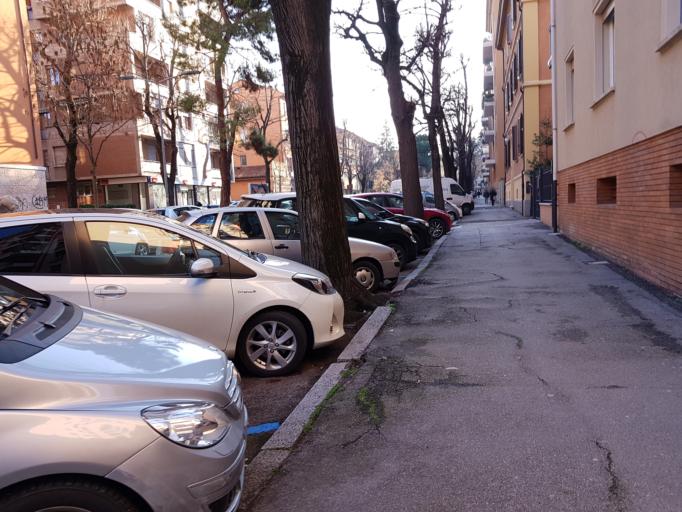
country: IT
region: Emilia-Romagna
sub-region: Provincia di Bologna
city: Bologna
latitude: 44.4848
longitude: 11.3599
